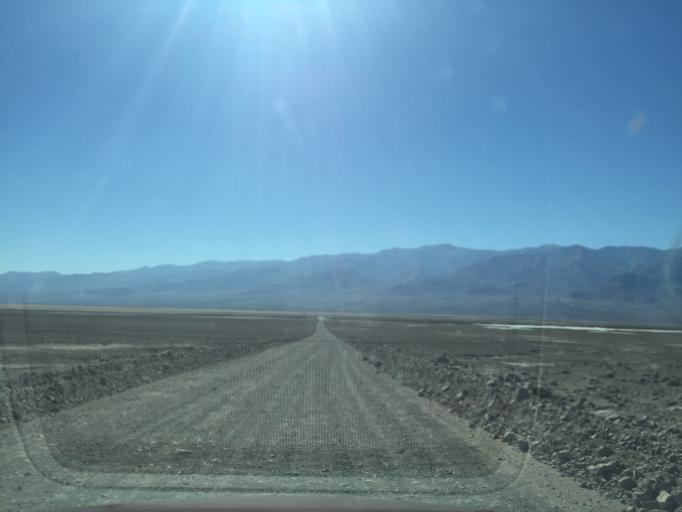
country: US
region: Nevada
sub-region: Nye County
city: Beatty
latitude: 36.2978
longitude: -116.8130
